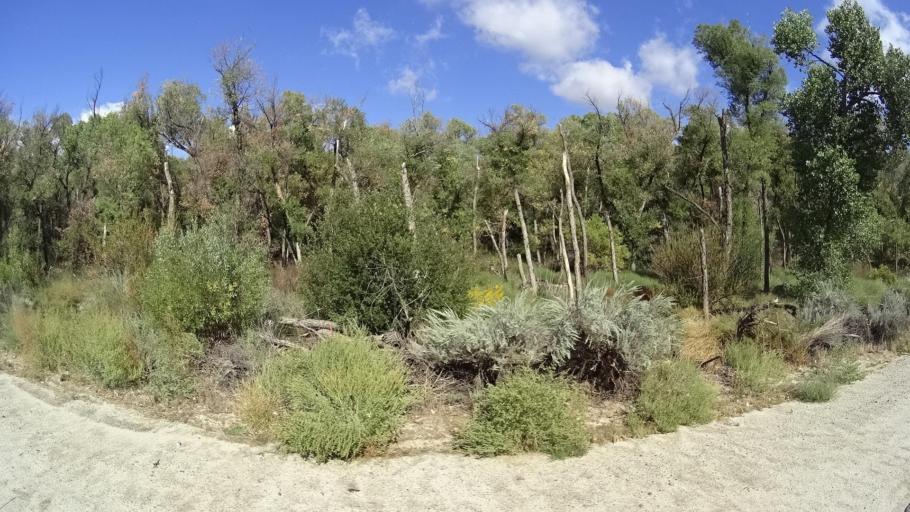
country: US
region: California
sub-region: San Diego County
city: Campo
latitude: 32.7095
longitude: -116.4925
